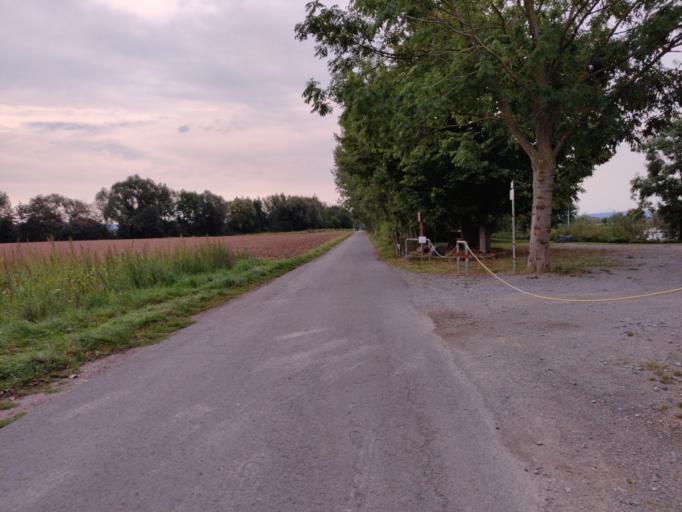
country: DE
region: Lower Saxony
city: Hameln
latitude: 52.0826
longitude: 9.3690
